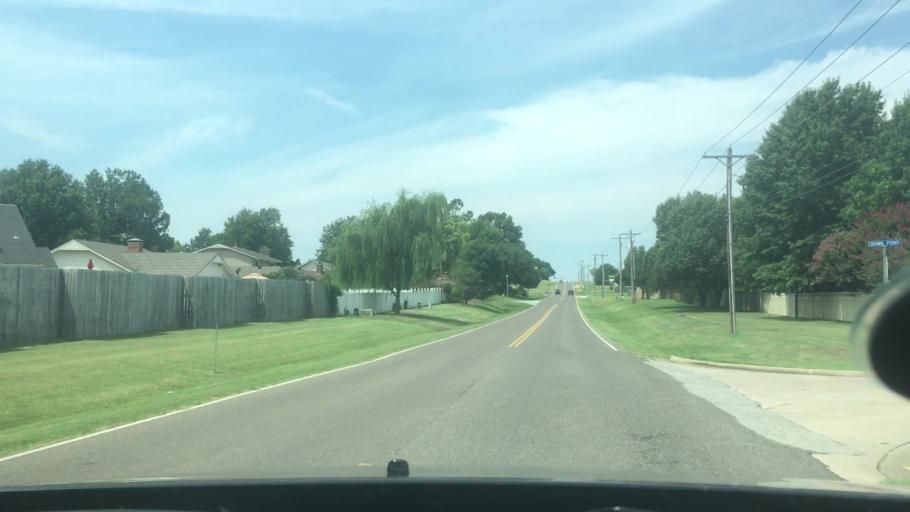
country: US
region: Oklahoma
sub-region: Pottawatomie County
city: Shawnee
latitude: 35.3617
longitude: -96.9046
